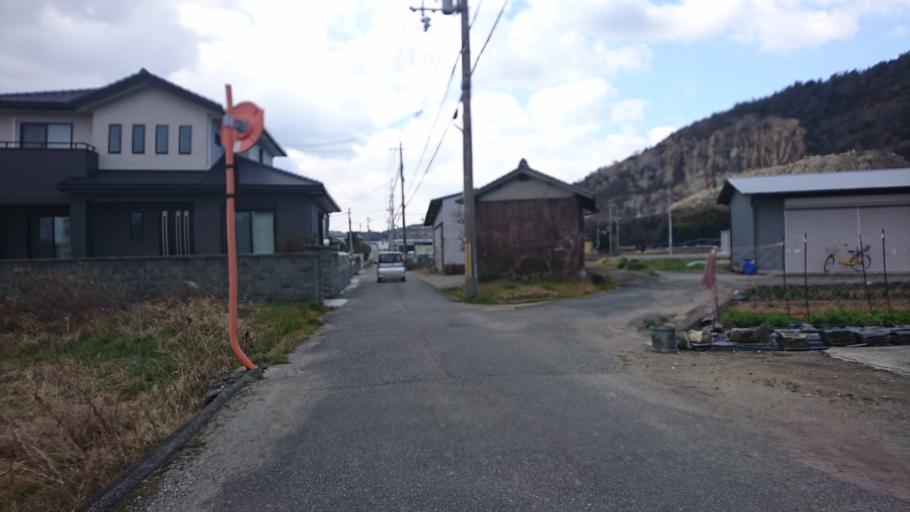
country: JP
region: Hyogo
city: Kakogawacho-honmachi
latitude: 34.7953
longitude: 134.8030
